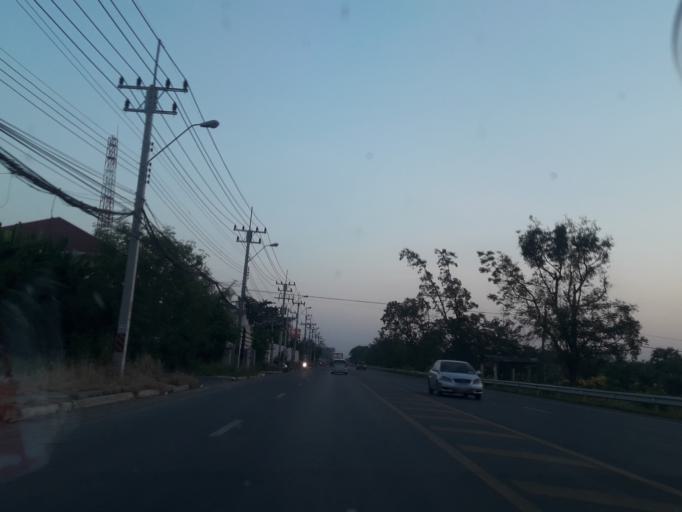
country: TH
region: Pathum Thani
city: Khlong Luang
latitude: 14.0886
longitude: 100.7103
